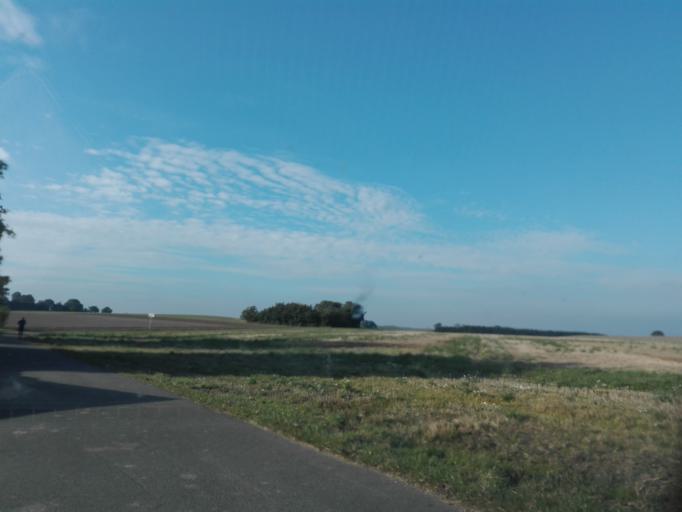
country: DK
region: Central Jutland
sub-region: Odder Kommune
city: Odder
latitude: 55.9306
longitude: 10.1912
